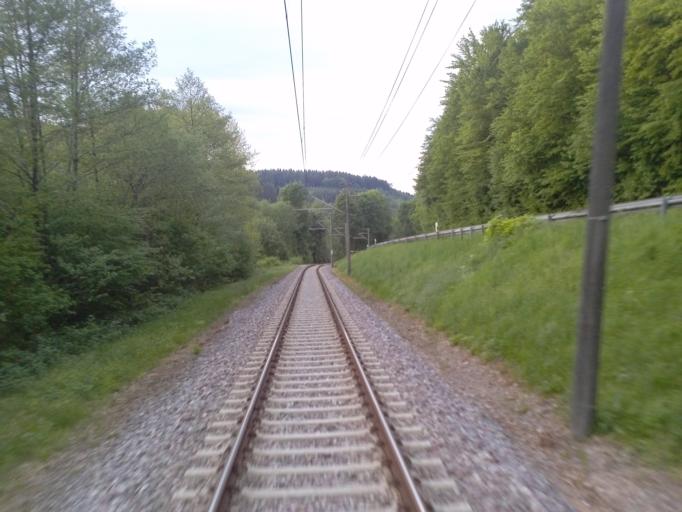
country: DE
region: Baden-Wuerttemberg
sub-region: Karlsruhe Region
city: Ettlingen
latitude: 48.8925
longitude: 8.4504
